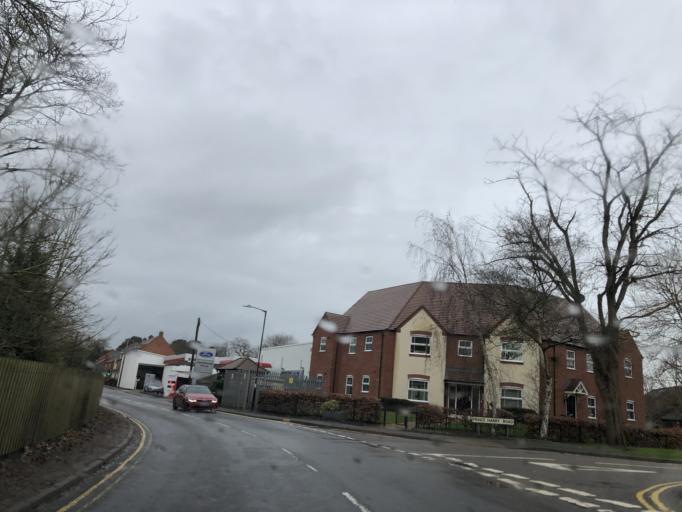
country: GB
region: England
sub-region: Warwickshire
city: Henley in Arden
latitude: 52.2874
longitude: -1.7767
